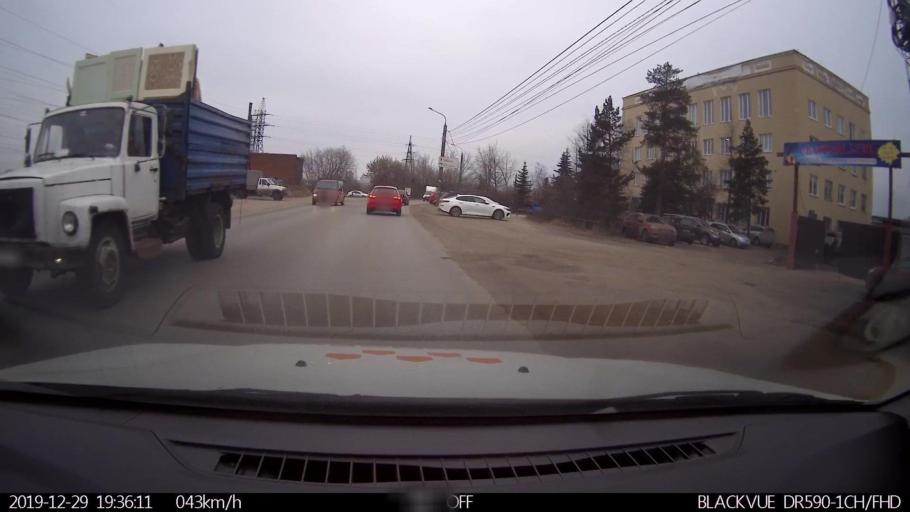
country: RU
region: Nizjnij Novgorod
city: Neklyudovo
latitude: 56.3463
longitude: 43.8911
